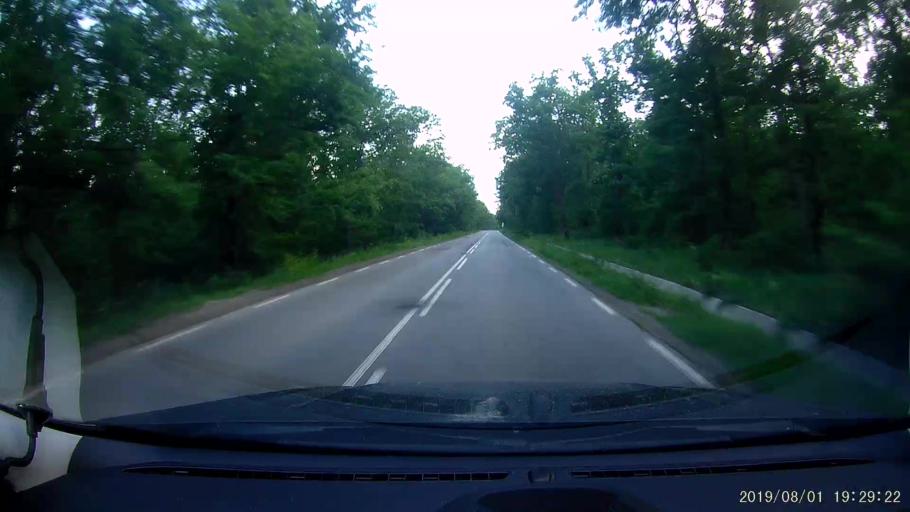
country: BG
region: Burgas
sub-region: Obshtina Sungurlare
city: Sungurlare
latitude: 42.8269
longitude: 26.9080
